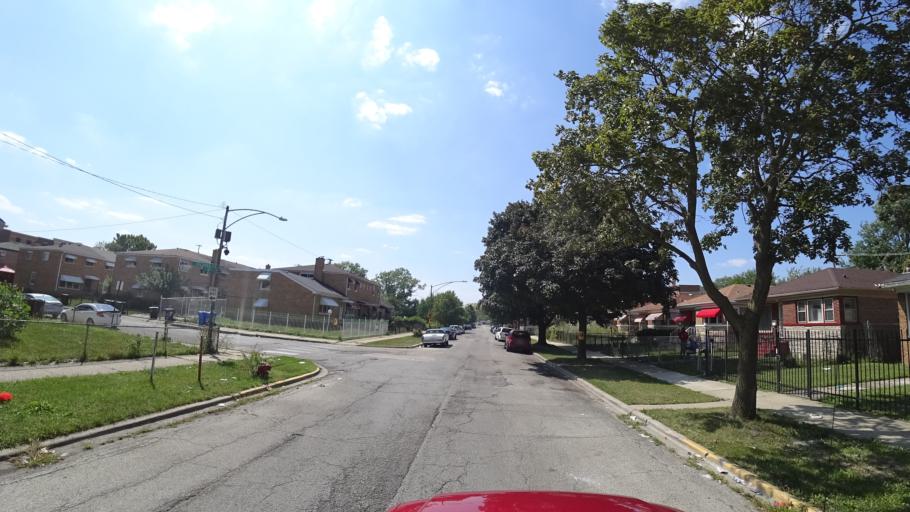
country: US
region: Illinois
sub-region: Cook County
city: Cicero
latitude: 41.8570
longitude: -87.7323
